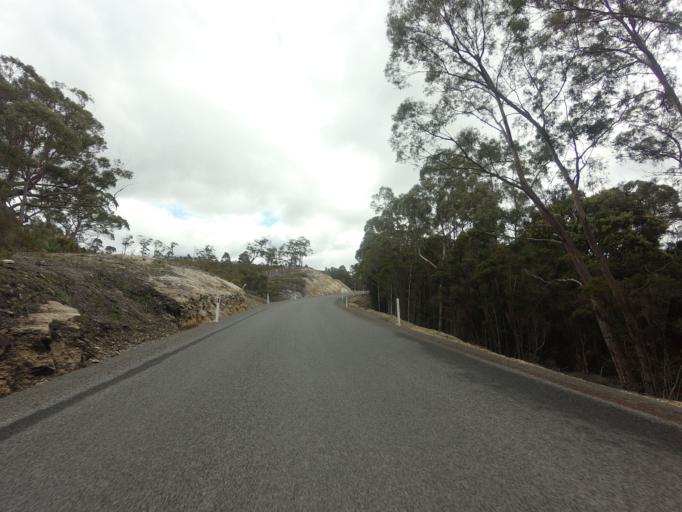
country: AU
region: Tasmania
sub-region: Huon Valley
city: Geeveston
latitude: -43.4266
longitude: 146.9057
